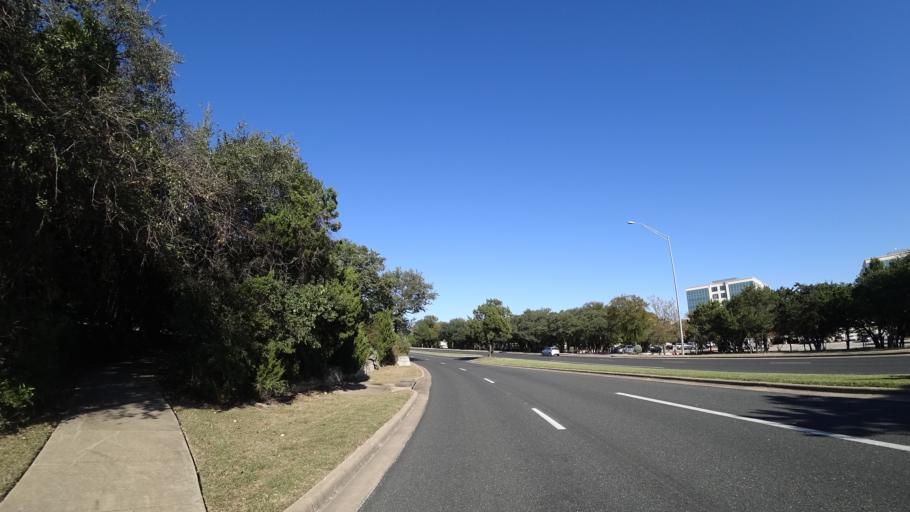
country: US
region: Texas
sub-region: Williamson County
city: Jollyville
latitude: 30.3861
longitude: -97.7389
